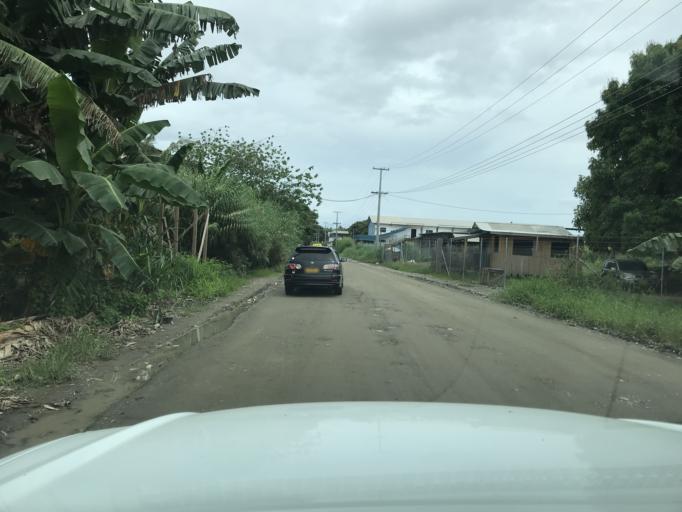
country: SB
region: Guadalcanal
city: Honiara
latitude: -9.4304
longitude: 160.0365
